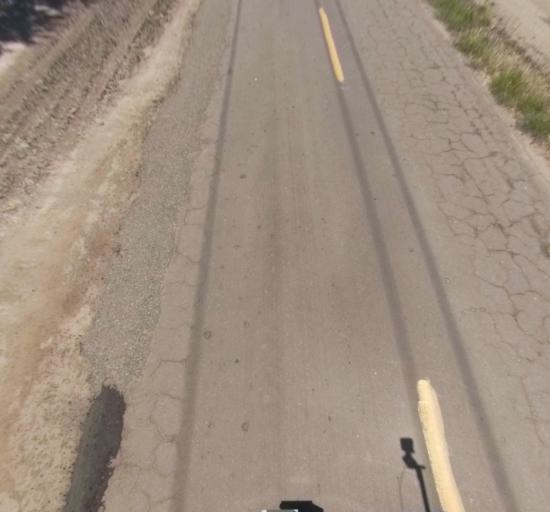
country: US
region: California
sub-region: Madera County
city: Chowchilla
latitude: 37.0640
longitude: -120.3288
